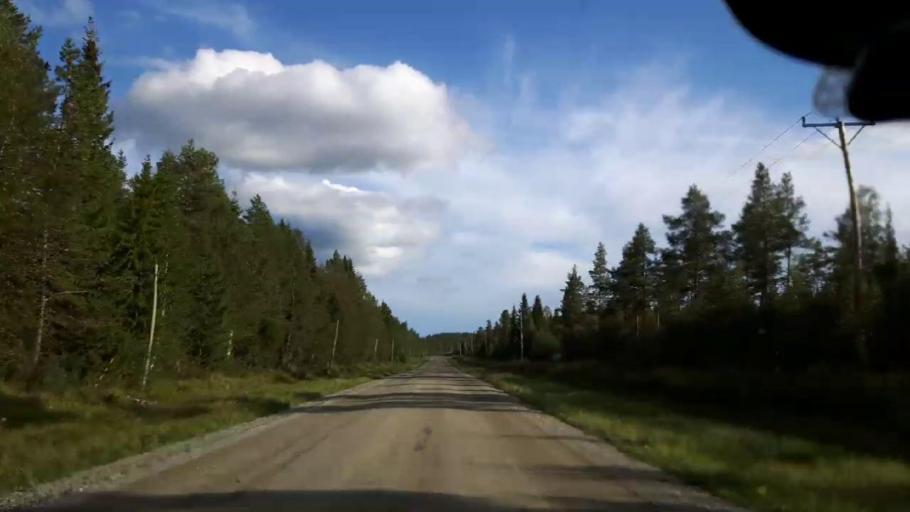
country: SE
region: Jaemtland
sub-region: Stroemsunds Kommun
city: Stroemsund
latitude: 63.3042
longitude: 15.5547
